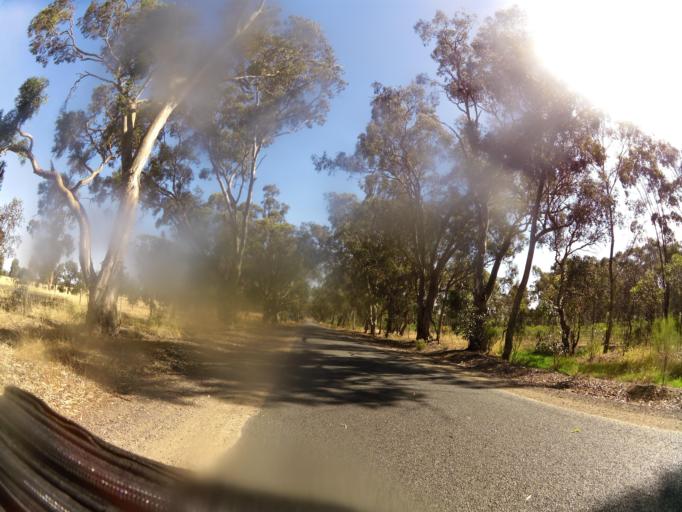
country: AU
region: Victoria
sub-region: Campaspe
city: Kyabram
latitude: -36.8727
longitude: 145.0861
